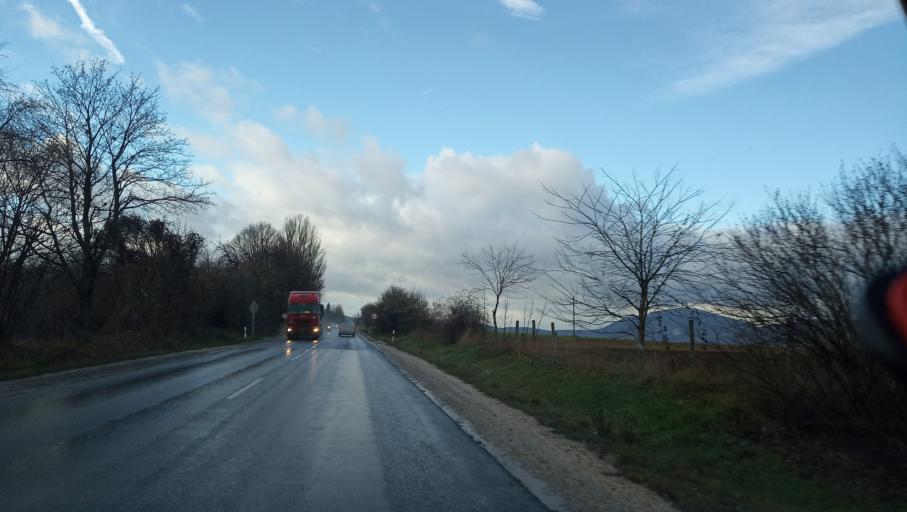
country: HU
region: Pest
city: Solymar
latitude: 47.6064
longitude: 18.9460
